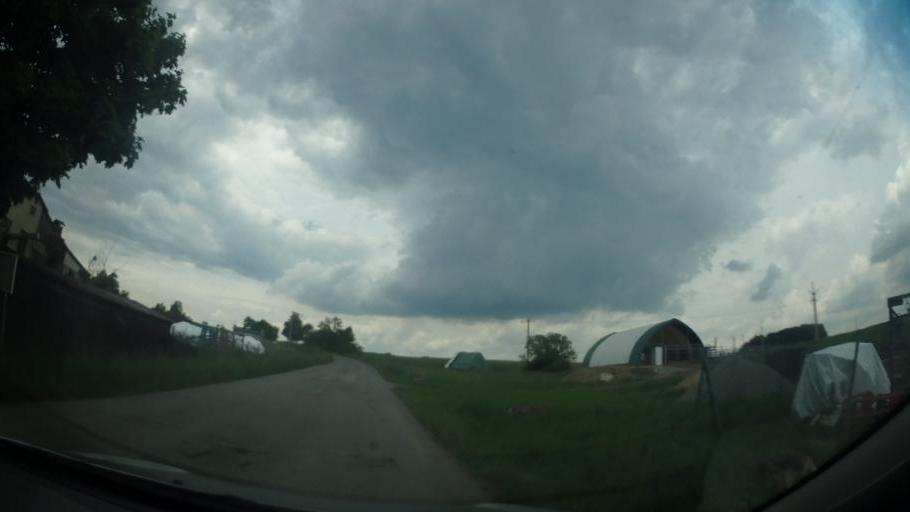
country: CZ
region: South Moravian
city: Olesnice
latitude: 49.4877
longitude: 16.4207
